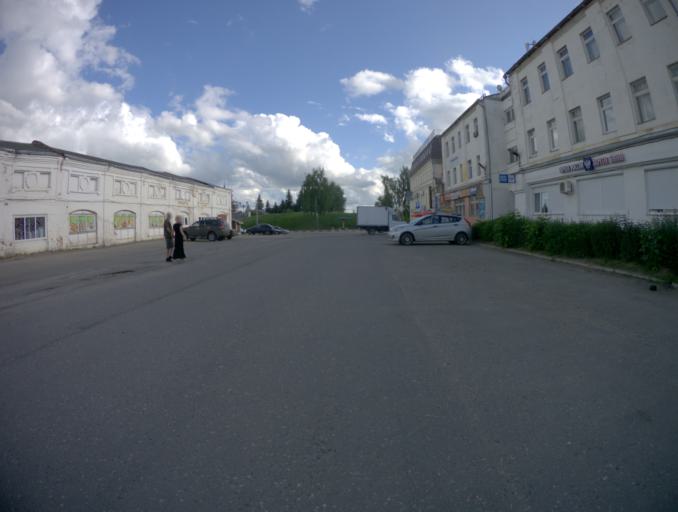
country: RU
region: Vladimir
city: Yur'yev-Pol'skiy
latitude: 56.4998
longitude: 39.6803
